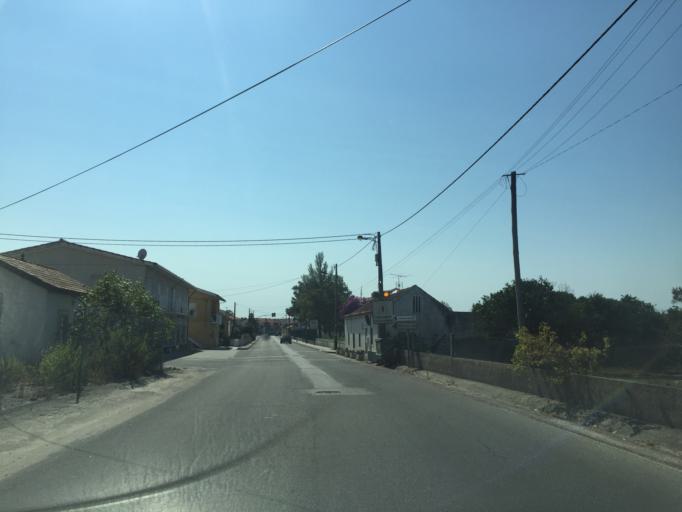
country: PT
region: Coimbra
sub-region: Montemor-O-Velho
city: Arazede
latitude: 40.3149
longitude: -8.7473
